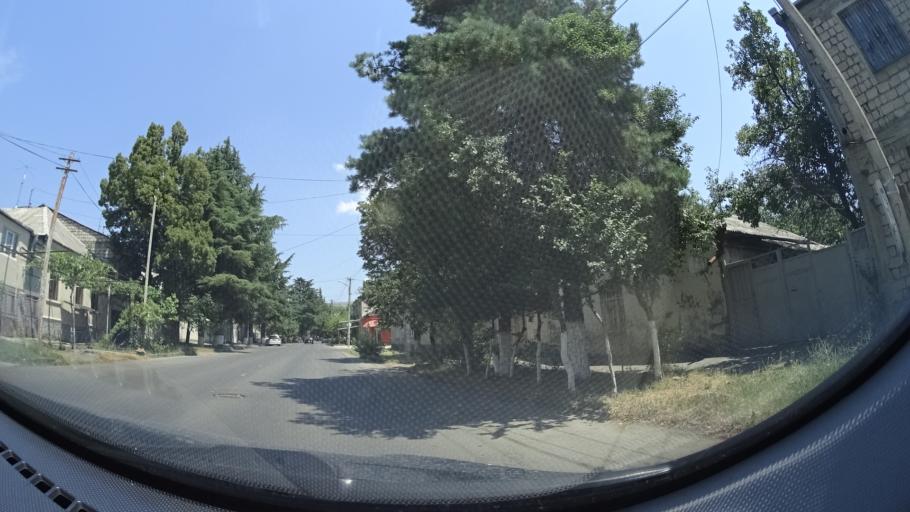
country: GE
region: Shida Kartli
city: Gori
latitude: 41.9889
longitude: 44.1178
